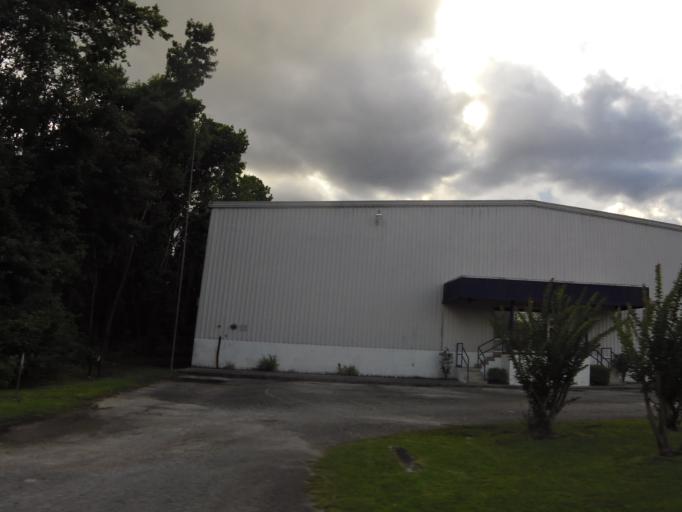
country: US
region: Florida
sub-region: Duval County
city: Jacksonville
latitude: 30.3190
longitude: -81.7645
